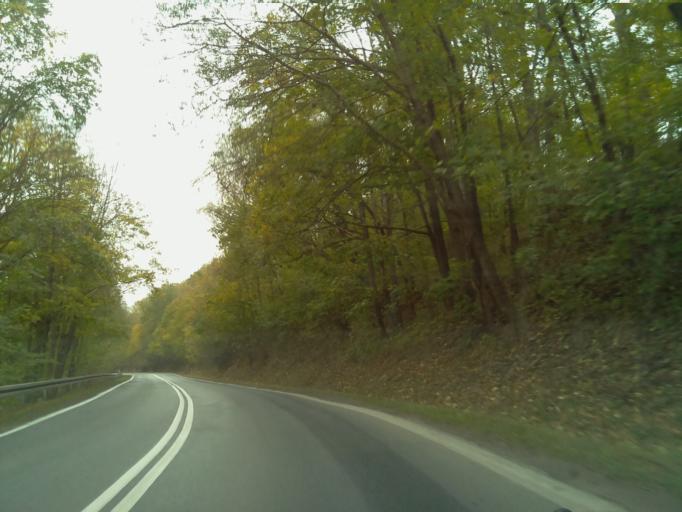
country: PL
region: Lower Silesian Voivodeship
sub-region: Powiat jaworski
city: Bolkow
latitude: 50.9242
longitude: 16.0920
